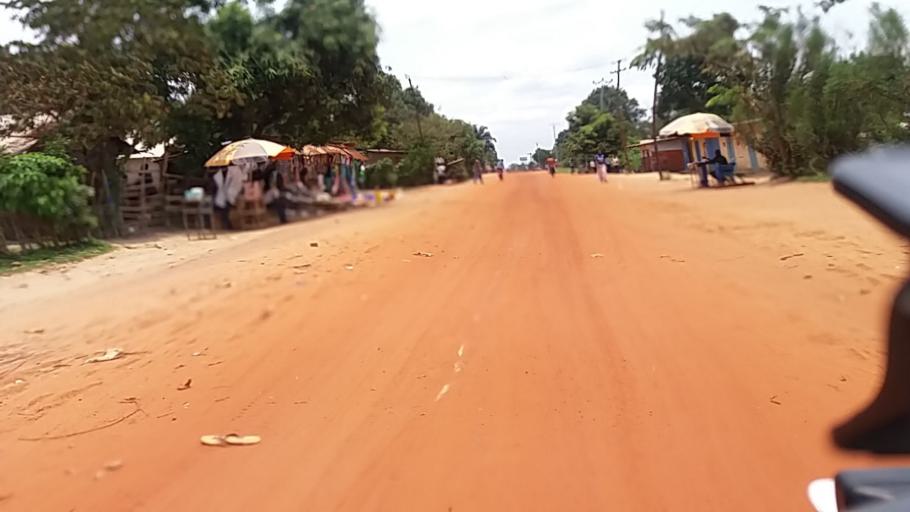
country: CD
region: Bandundu
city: Bandundu
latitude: -3.3206
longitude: 17.3943
